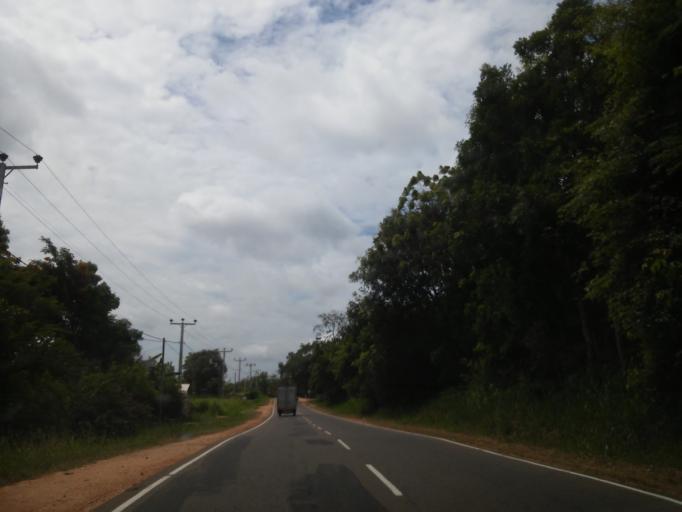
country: LK
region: Central
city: Sigiriya
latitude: 8.0463
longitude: 80.7315
